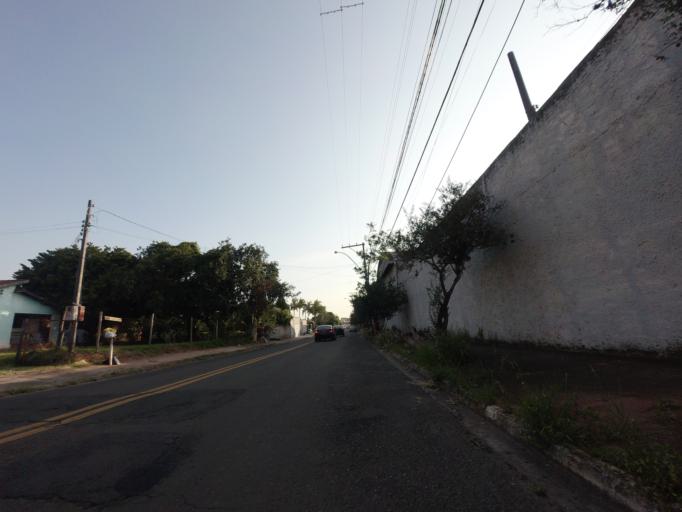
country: BR
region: Sao Paulo
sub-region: Piracicaba
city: Piracicaba
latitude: -22.7379
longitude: -47.6095
